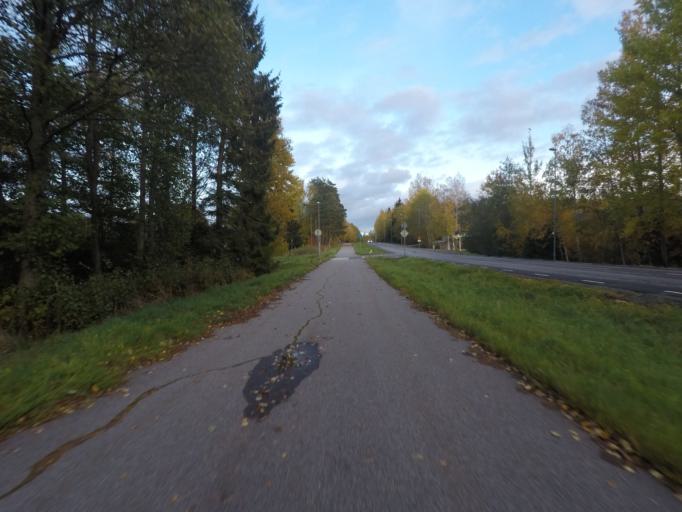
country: SE
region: OErebro
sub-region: Karlskoga Kommun
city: Karlskoga
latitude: 59.3067
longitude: 14.4753
